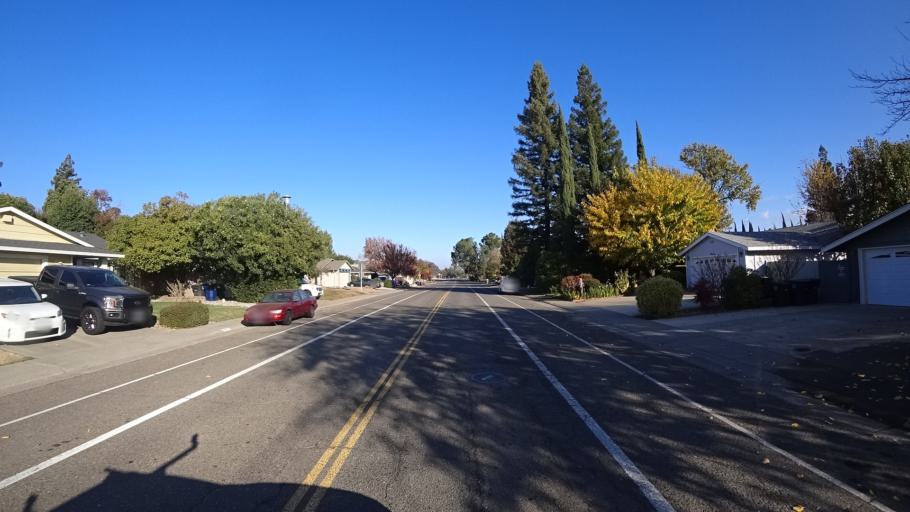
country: US
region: California
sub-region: Sacramento County
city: Citrus Heights
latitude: 38.7085
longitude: -121.2536
